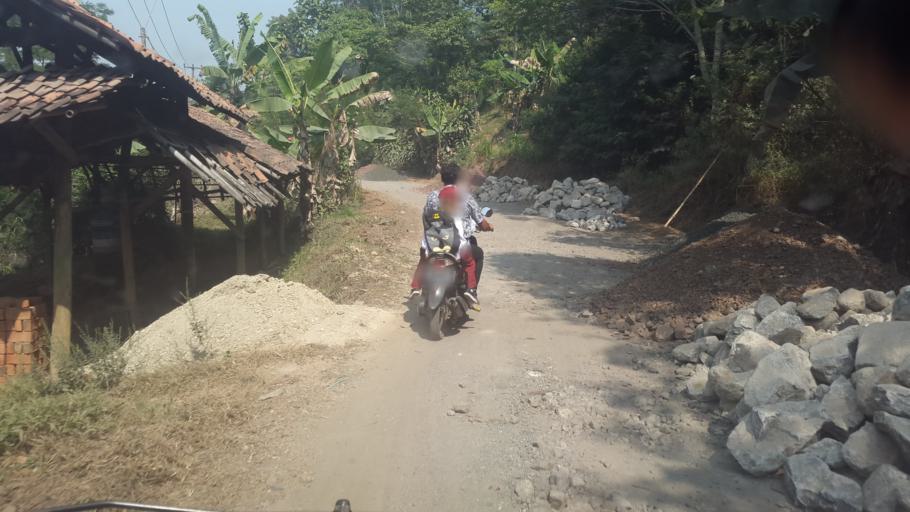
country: ID
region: West Java
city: Pasirreungit
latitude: -6.9355
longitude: 107.0085
